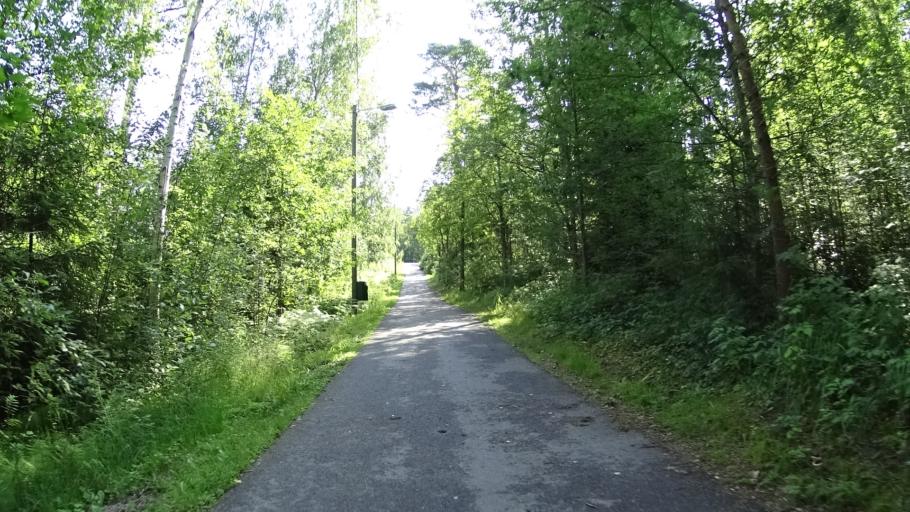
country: FI
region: Uusimaa
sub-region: Helsinki
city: Kauniainen
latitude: 60.2207
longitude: 24.7059
